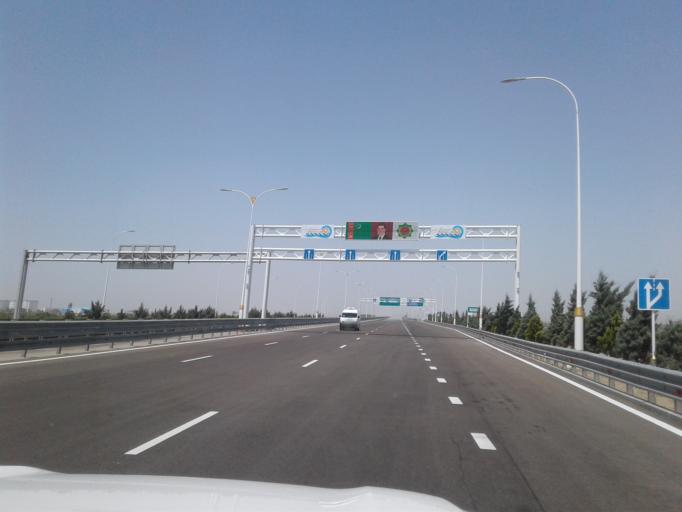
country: TM
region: Balkan
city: Turkmenbasy
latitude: 39.9770
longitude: 52.8687
